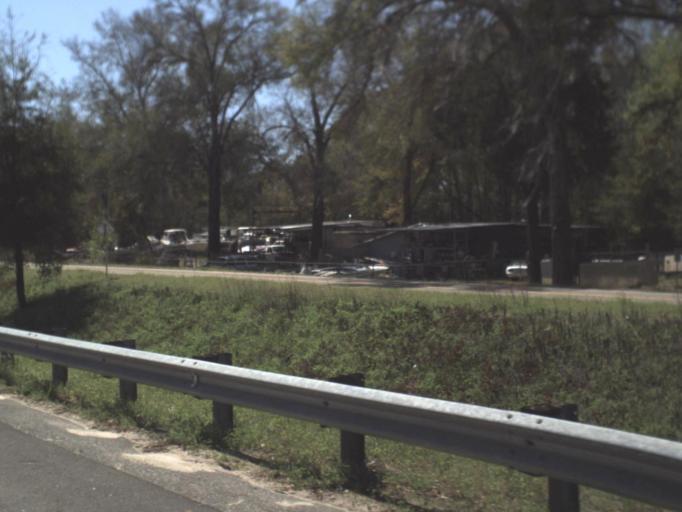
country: US
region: Florida
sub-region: Leon County
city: Tallahassee
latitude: 30.3813
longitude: -84.2727
